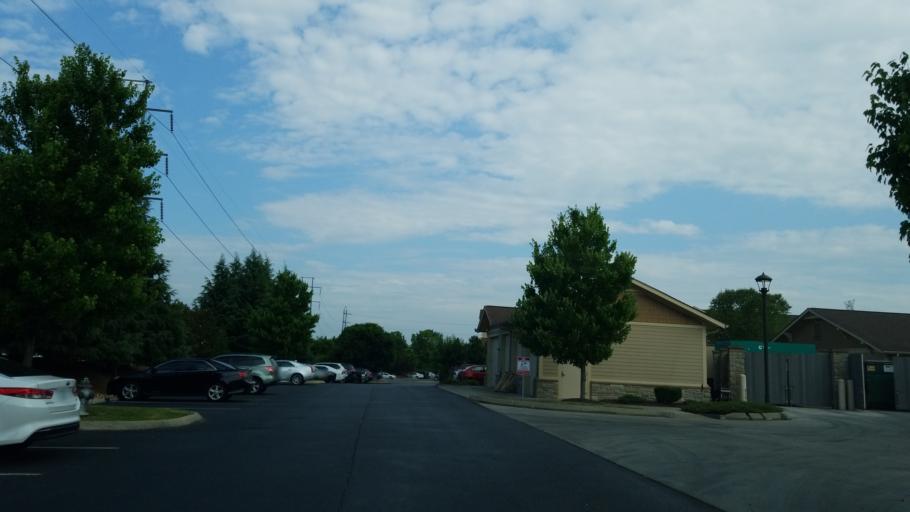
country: US
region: Tennessee
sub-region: Rutherford County
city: La Vergne
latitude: 36.0288
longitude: -86.5886
